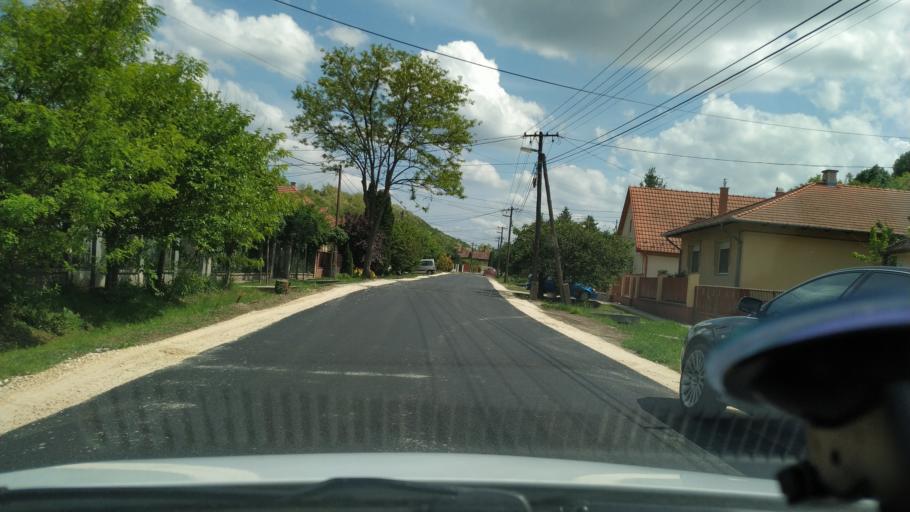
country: HU
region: Pest
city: Mende
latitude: 47.4243
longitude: 19.4465
